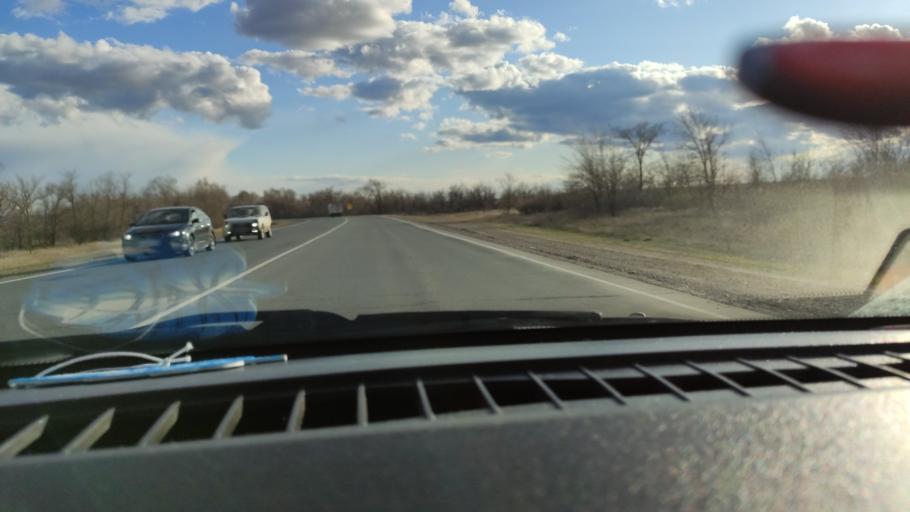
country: RU
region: Saratov
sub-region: Saratovskiy Rayon
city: Saratov
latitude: 51.7048
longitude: 46.0134
